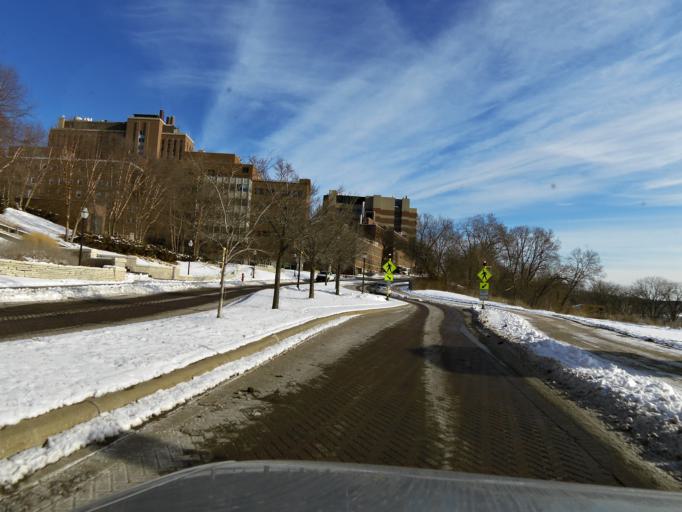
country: US
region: Minnesota
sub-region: Hennepin County
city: Minneapolis
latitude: 44.9713
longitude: -93.2359
